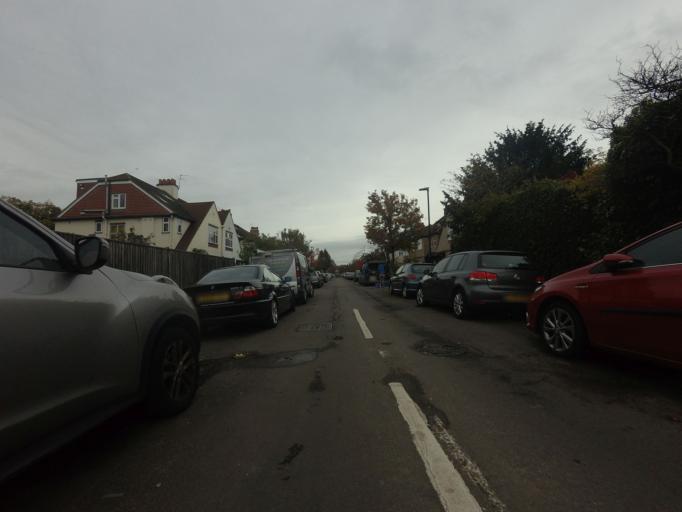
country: GB
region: England
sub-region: Greater London
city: Teddington
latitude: 51.4212
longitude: -0.3334
